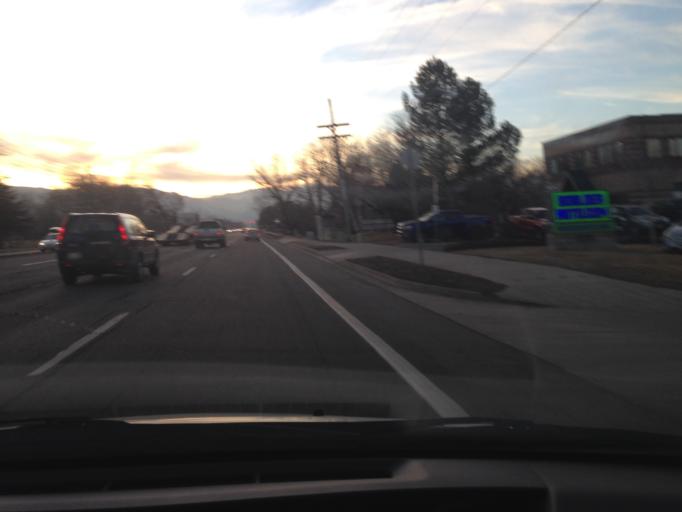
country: US
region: Colorado
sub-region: Boulder County
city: Boulder
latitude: 40.0151
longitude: -105.2188
